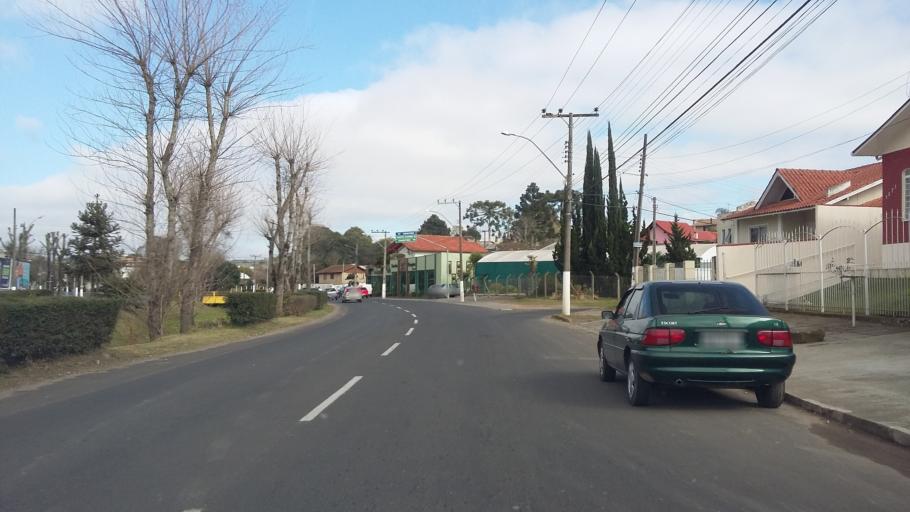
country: BR
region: Santa Catarina
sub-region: Lages
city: Lages
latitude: -27.8130
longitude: -50.3356
